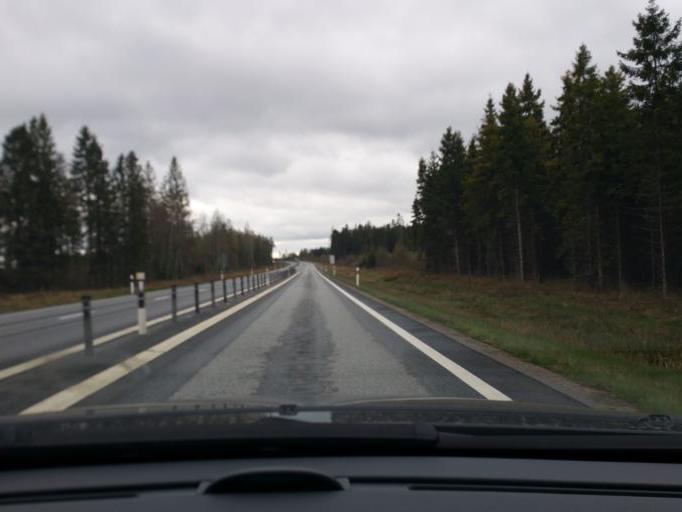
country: SE
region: Kronoberg
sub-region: Vaxjo Kommun
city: Vaexjoe
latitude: 56.9333
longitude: 14.7227
